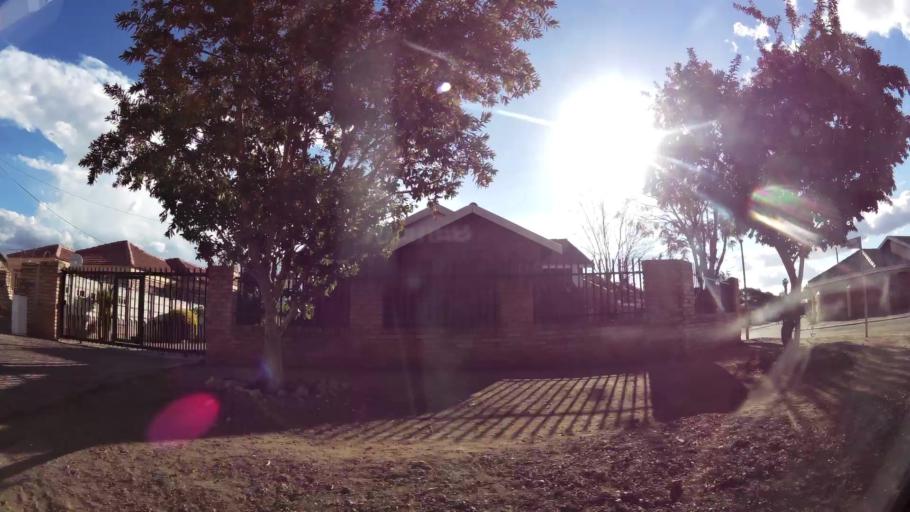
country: ZA
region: Limpopo
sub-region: Capricorn District Municipality
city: Polokwane
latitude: -23.9343
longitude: 29.4515
